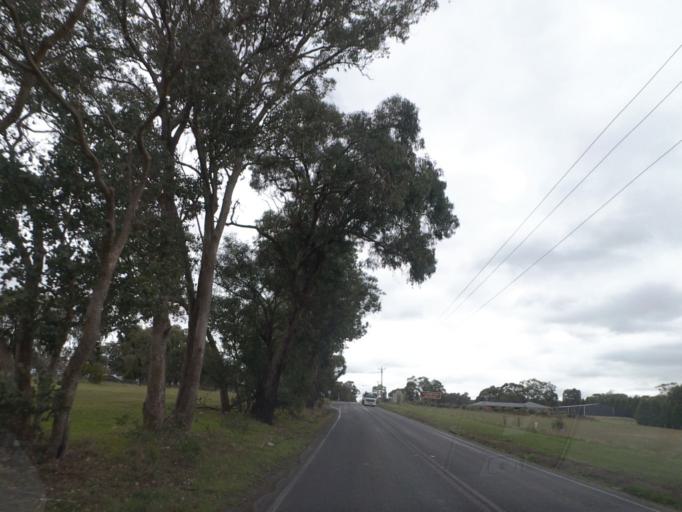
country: AU
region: Victoria
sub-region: Nillumbik
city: Doreen
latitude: -37.6278
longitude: 145.1342
